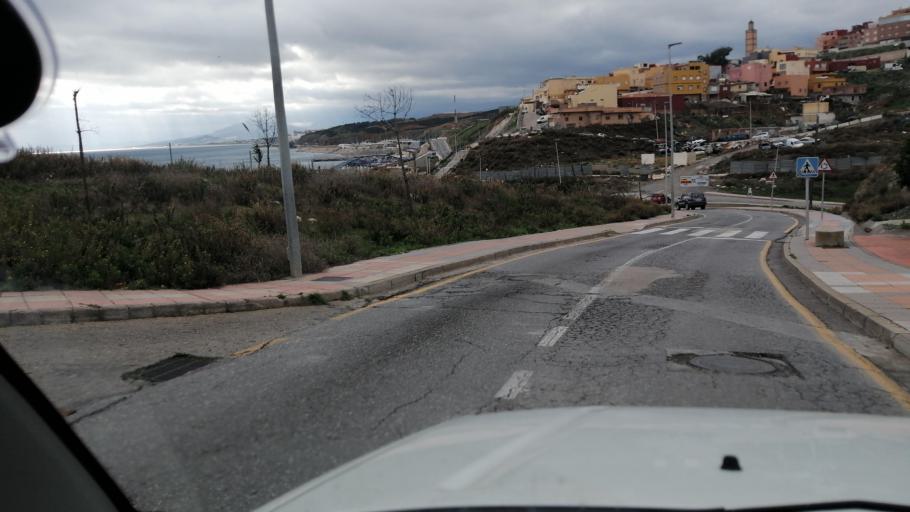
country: ES
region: Ceuta
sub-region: Ceuta
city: Ceuta
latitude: 35.8781
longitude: -5.3405
